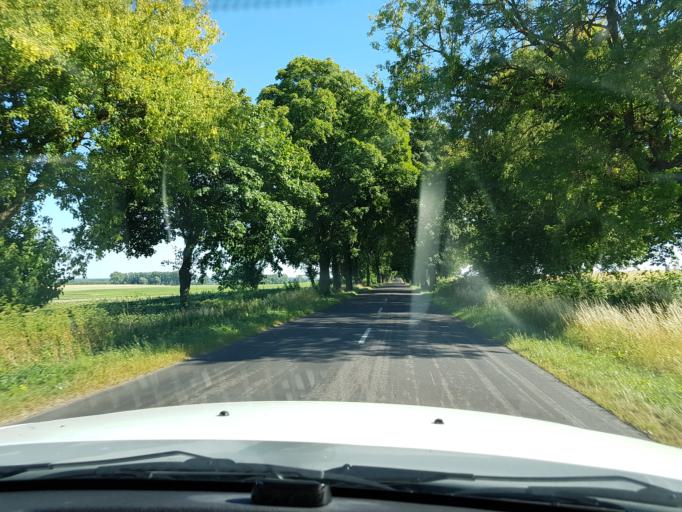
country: PL
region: West Pomeranian Voivodeship
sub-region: Powiat lobeski
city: Lobez
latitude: 53.6609
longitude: 15.6105
